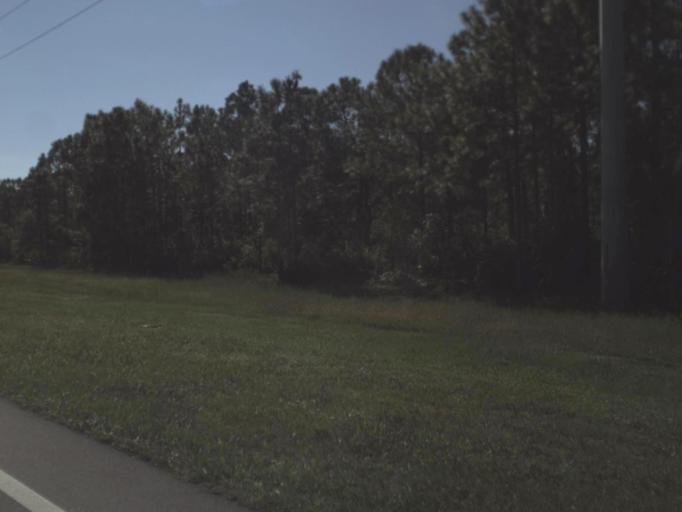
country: US
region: Florida
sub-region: Lee County
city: Gateway
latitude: 26.5862
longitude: -81.7240
